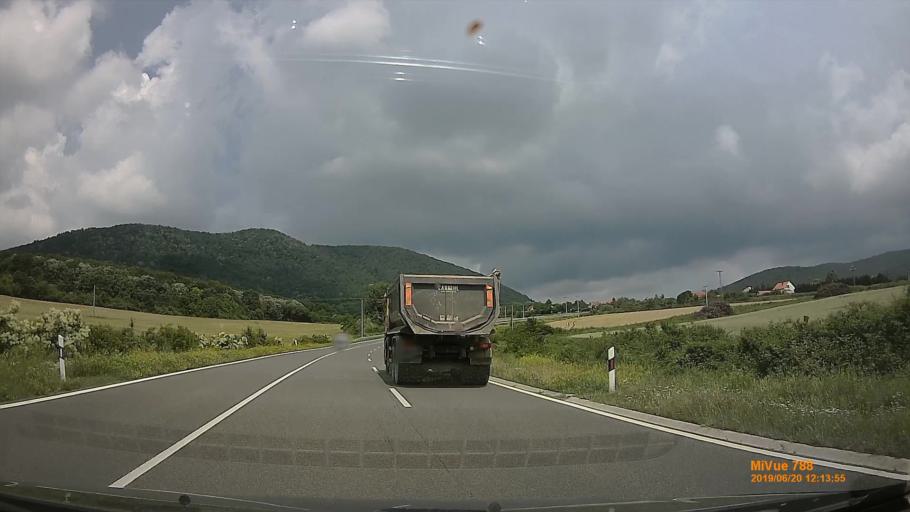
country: HU
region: Baranya
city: Hosszuheteny
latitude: 46.1629
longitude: 18.3423
